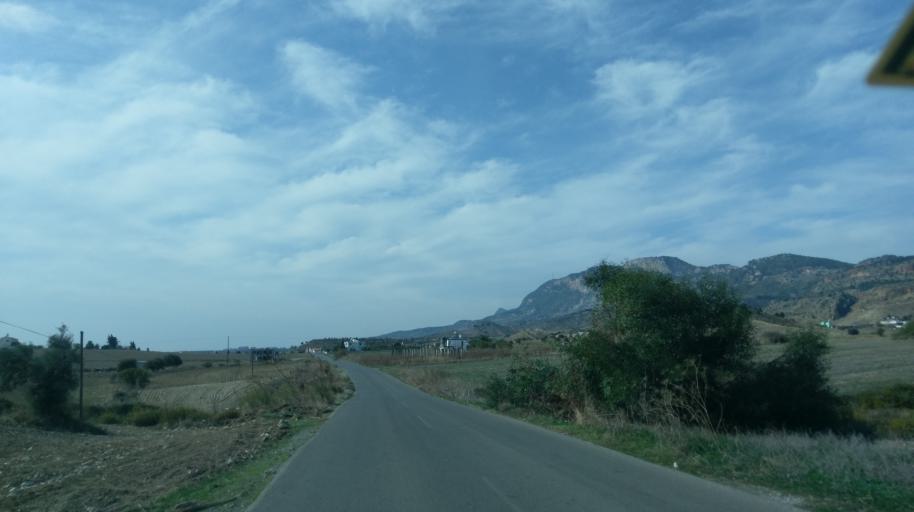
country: CY
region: Keryneia
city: Lapithos
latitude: 35.2817
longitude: 33.2228
